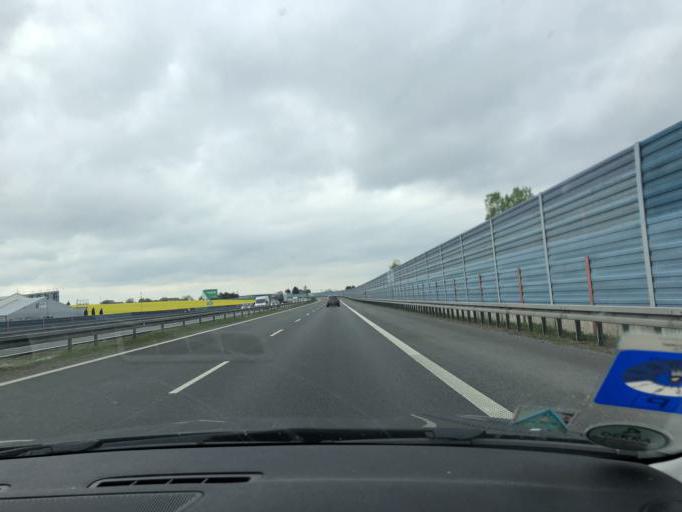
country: PL
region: Opole Voivodeship
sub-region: Powiat krapkowicki
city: Krapkowice
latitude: 50.5062
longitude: 17.9669
